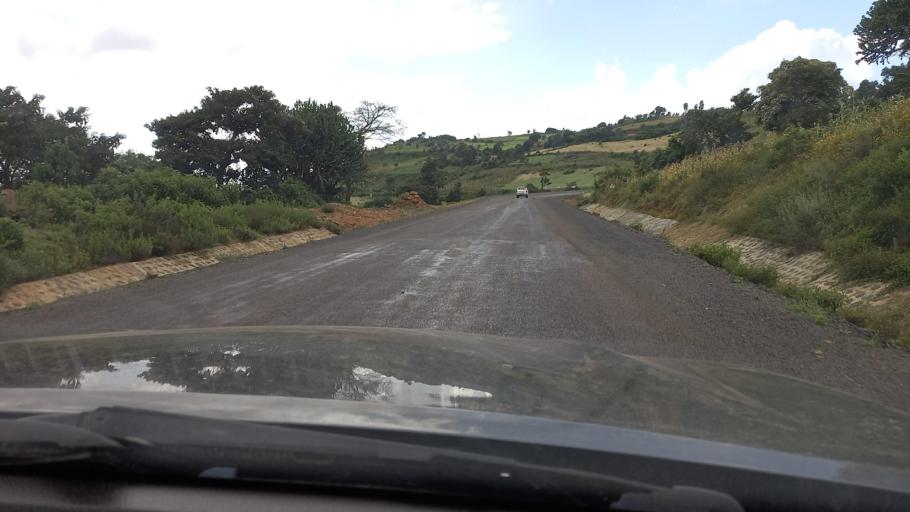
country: ET
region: Southern Nations, Nationalities, and People's Region
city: Mizan Teferi
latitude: 6.2148
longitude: 35.6382
